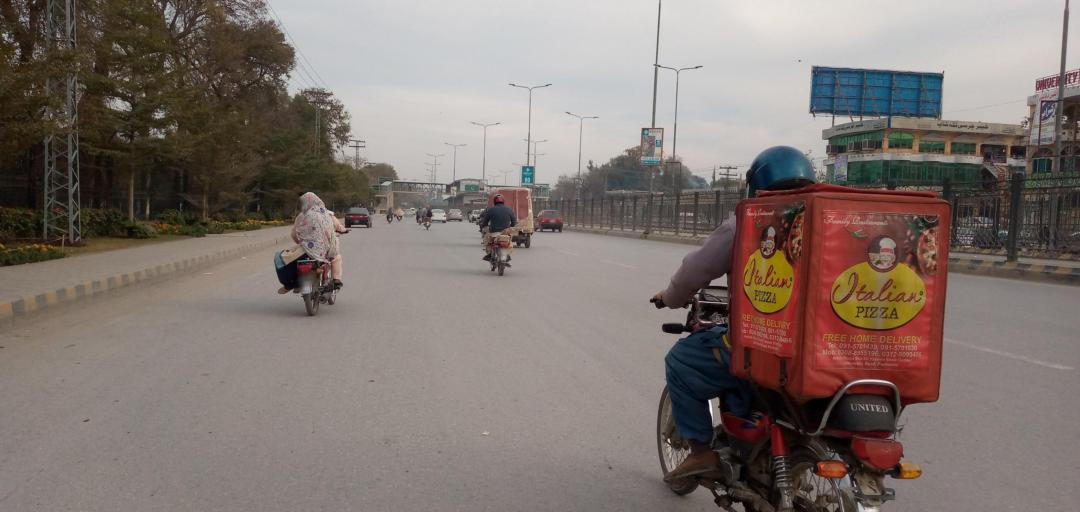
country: PK
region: Khyber Pakhtunkhwa
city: Peshawar
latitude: 33.9985
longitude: 71.4757
